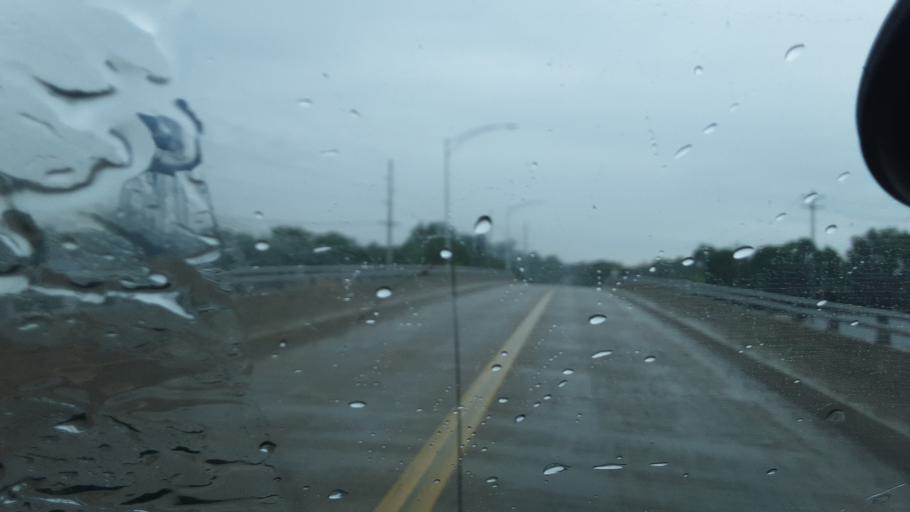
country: US
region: Ohio
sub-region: Williams County
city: Montpelier
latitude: 41.5788
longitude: -84.6073
